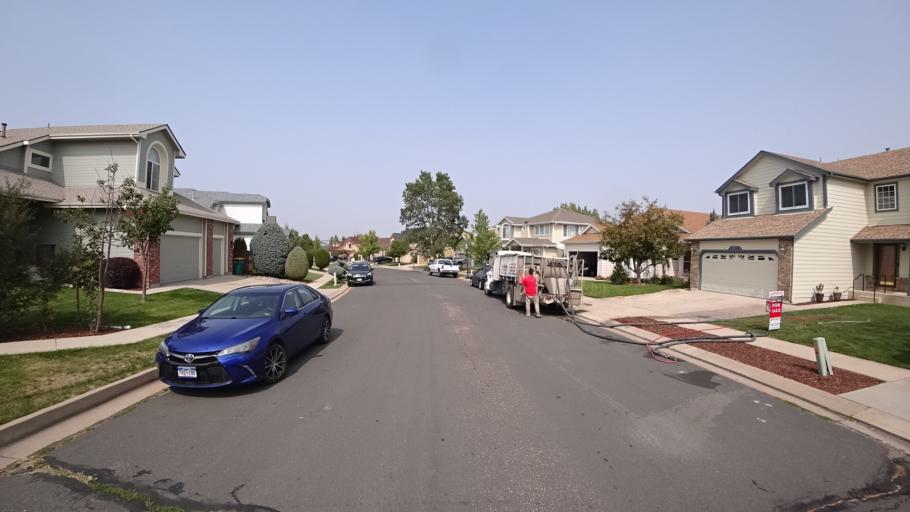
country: US
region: Colorado
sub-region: El Paso County
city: Cimarron Hills
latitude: 38.9193
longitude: -104.7336
